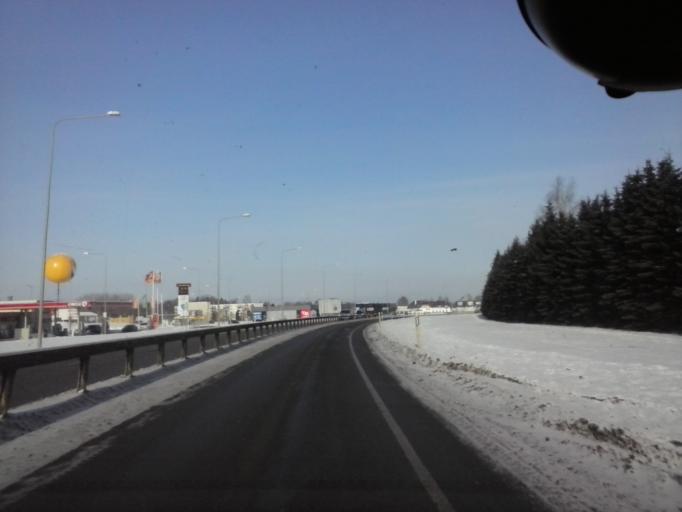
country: EE
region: Tartu
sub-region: Tartu linn
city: Tartu
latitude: 58.3596
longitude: 26.6791
